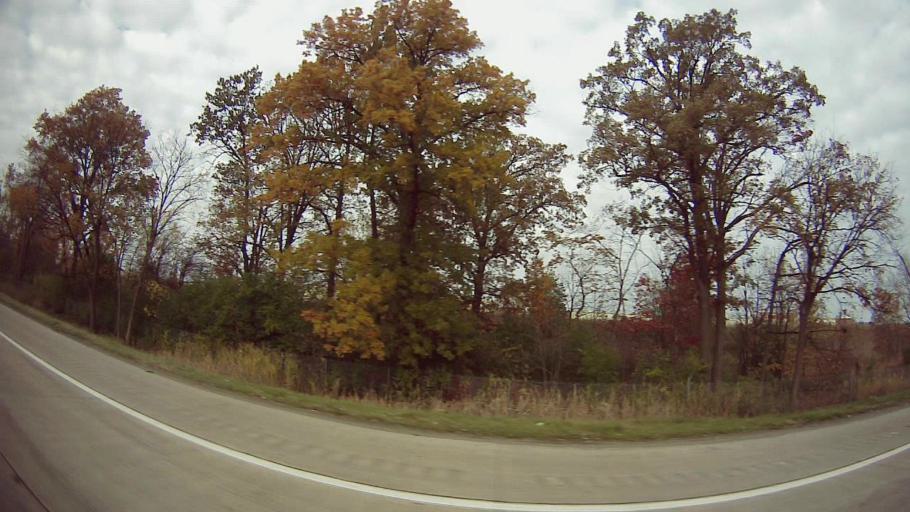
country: US
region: Michigan
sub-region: Wayne County
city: Allen Park
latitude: 42.2802
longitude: -83.2008
